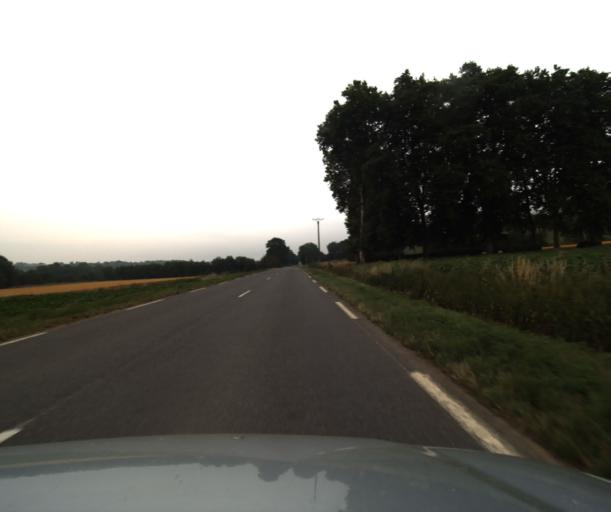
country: FR
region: Midi-Pyrenees
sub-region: Departement du Tarn-et-Garonne
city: Beaumont-de-Lomagne
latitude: 43.7930
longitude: 0.8942
